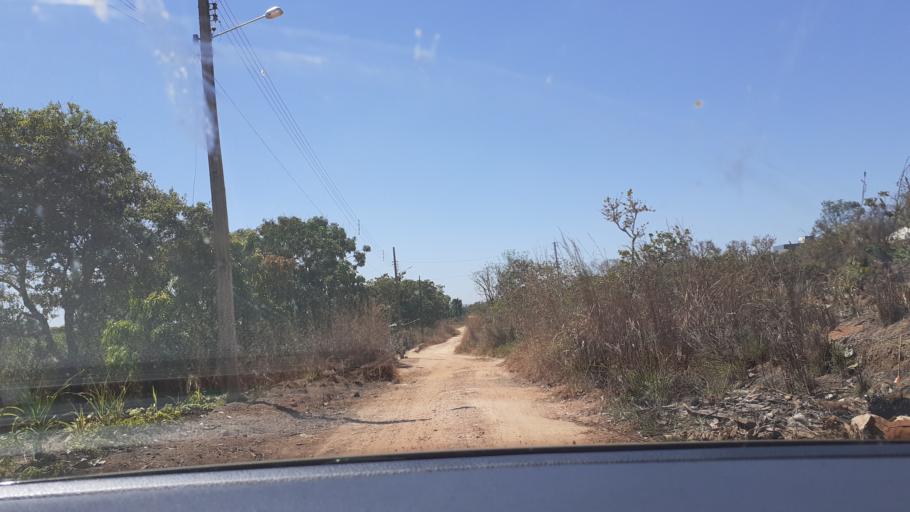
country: BR
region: Goias
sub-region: Caldas Novas
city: Caldas Novas
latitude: -17.7411
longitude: -48.6569
